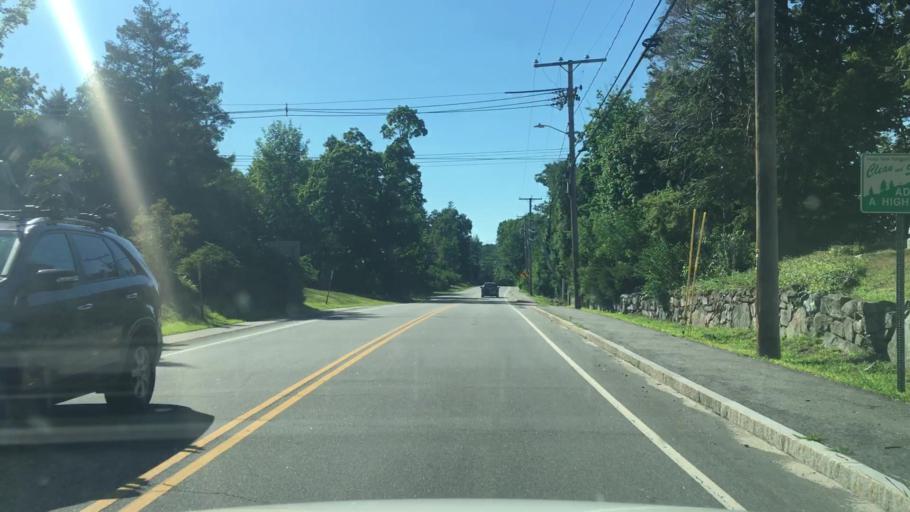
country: US
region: New Hampshire
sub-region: Rockingham County
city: Newmarket
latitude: 43.0354
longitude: -70.9444
